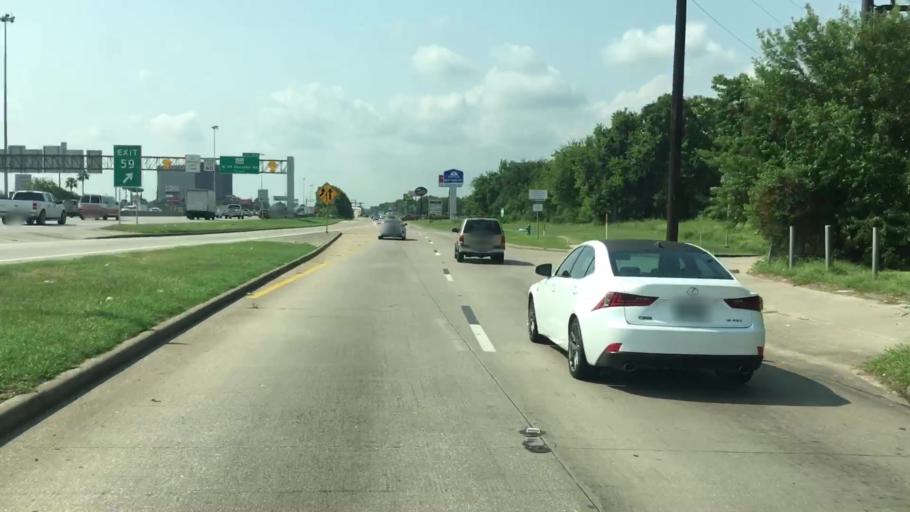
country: US
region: Texas
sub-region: Harris County
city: Aldine
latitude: 29.9301
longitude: -95.4099
